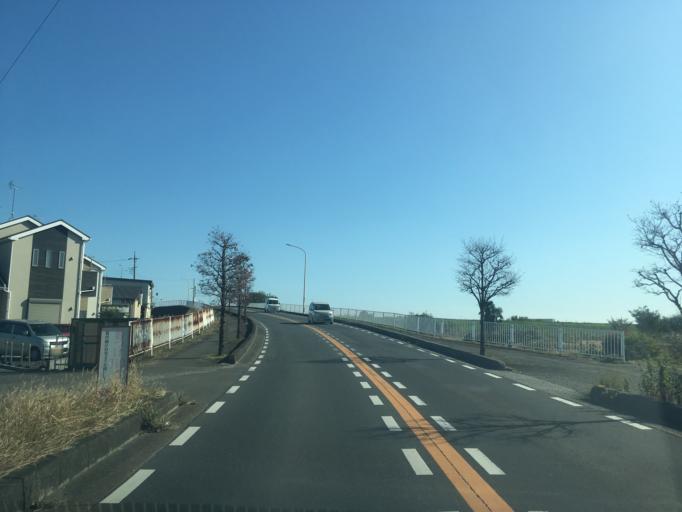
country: JP
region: Saitama
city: Kawagoe
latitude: 35.9425
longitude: 139.4642
